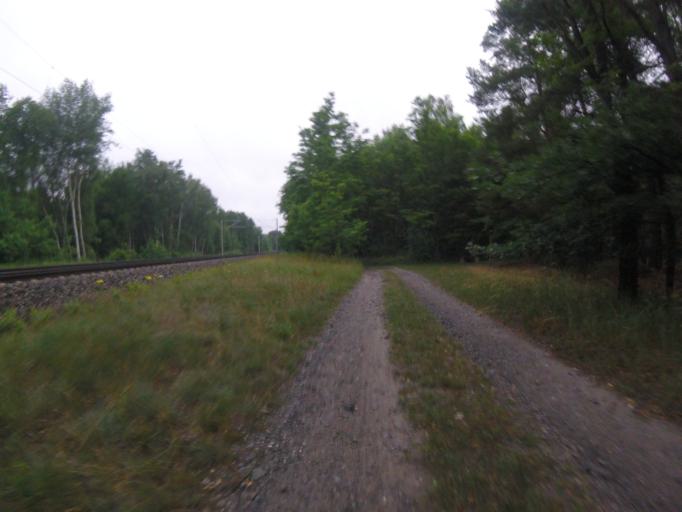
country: DE
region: Brandenburg
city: Bestensee
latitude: 52.2072
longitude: 13.6210
